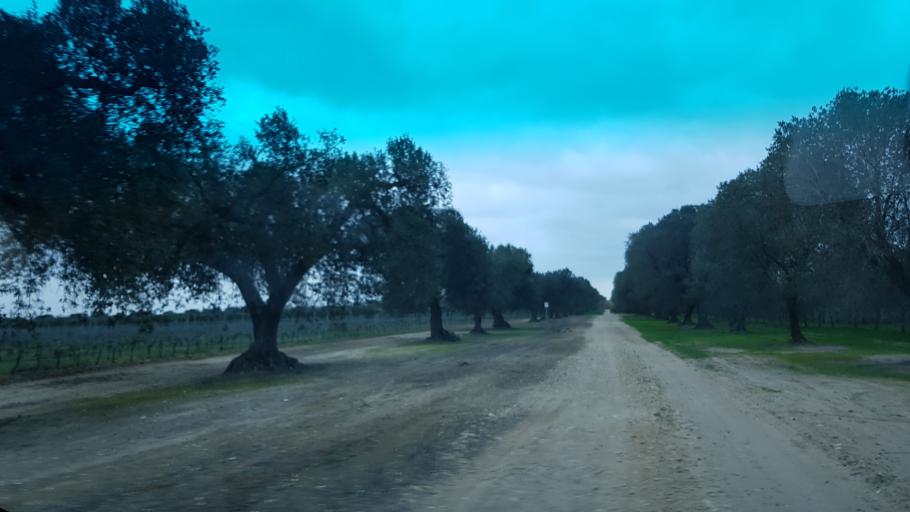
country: IT
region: Apulia
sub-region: Provincia di Brindisi
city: La Rosa
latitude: 40.5860
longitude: 17.9867
